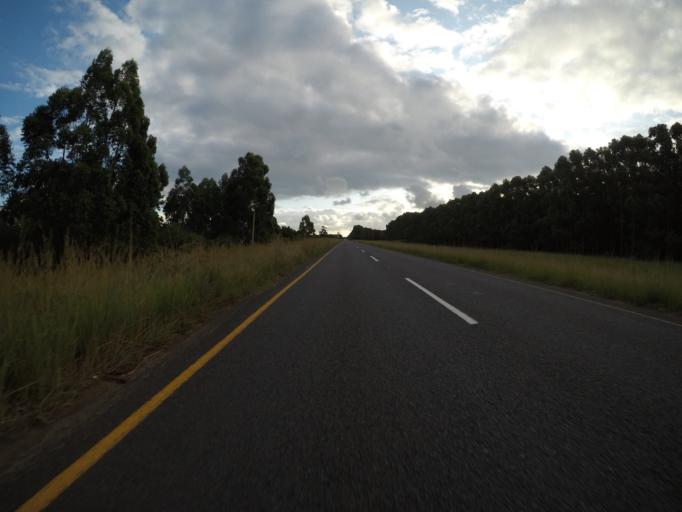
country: ZA
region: KwaZulu-Natal
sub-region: uMkhanyakude District Municipality
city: Mtubatuba
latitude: -28.3943
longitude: 32.2208
